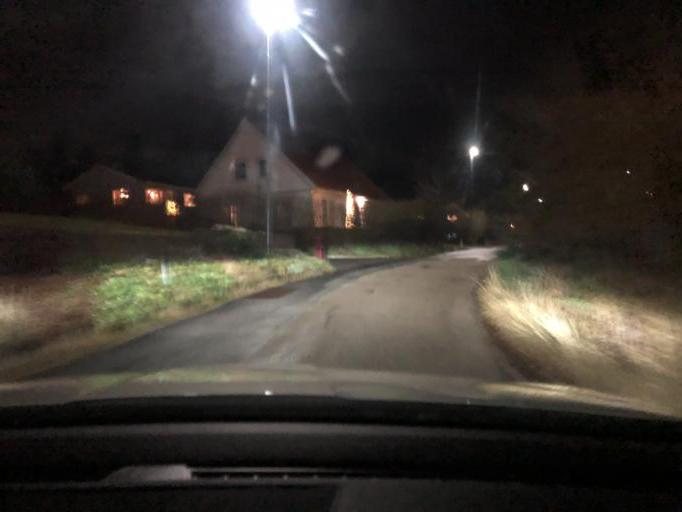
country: SE
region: Stockholm
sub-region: Jarfalla Kommun
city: Jakobsberg
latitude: 59.4657
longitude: 17.8246
